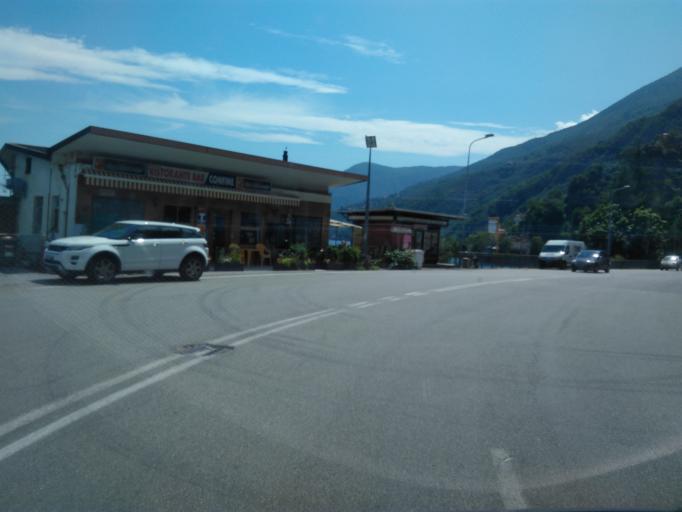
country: CH
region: Ticino
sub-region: Locarno District
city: Brissago
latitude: 46.1019
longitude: 8.6967
